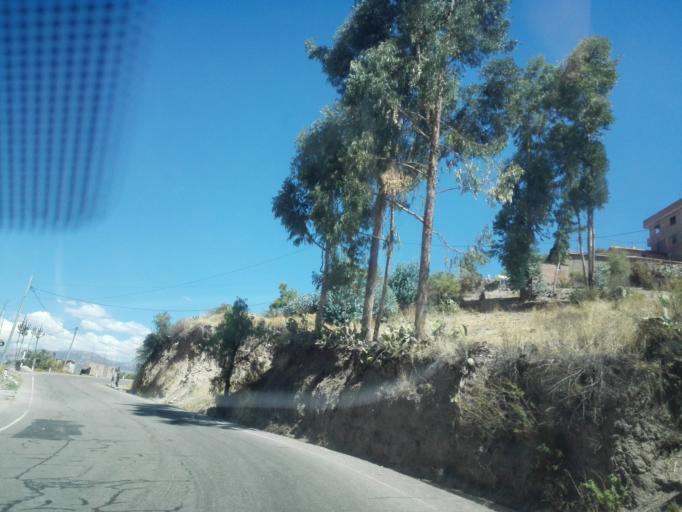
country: PE
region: Ayacucho
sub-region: Provincia de Huamanga
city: Ayacucho
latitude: -13.1654
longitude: -74.2448
